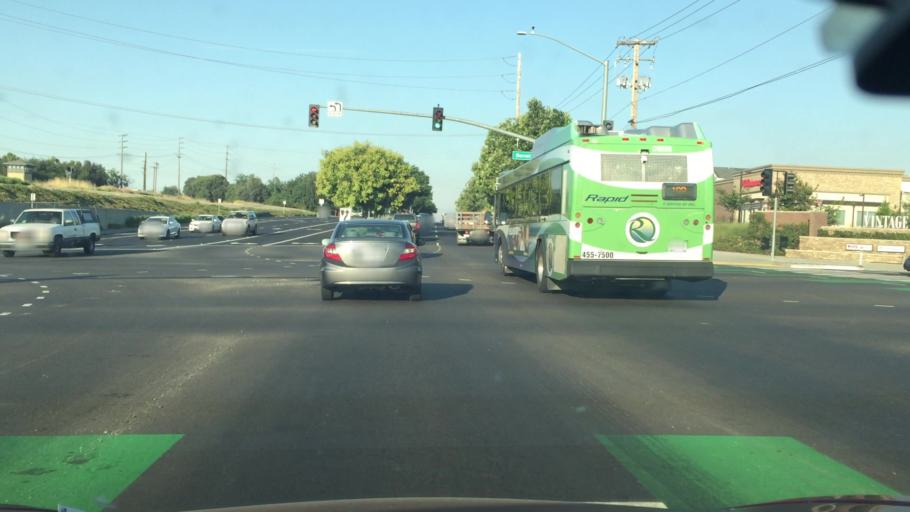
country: US
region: California
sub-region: Alameda County
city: Pleasanton
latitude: 37.6702
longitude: -121.8582
